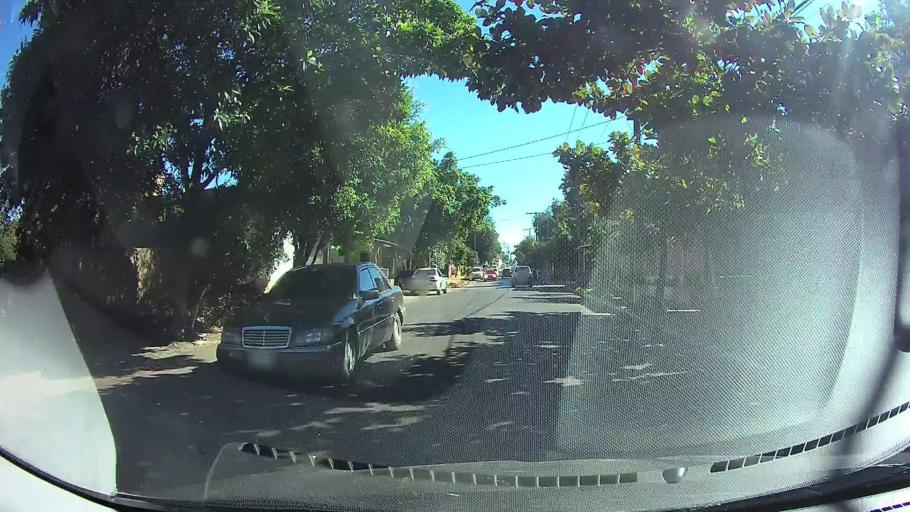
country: PY
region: Central
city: Villa Elisa
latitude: -25.3492
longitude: -57.5794
